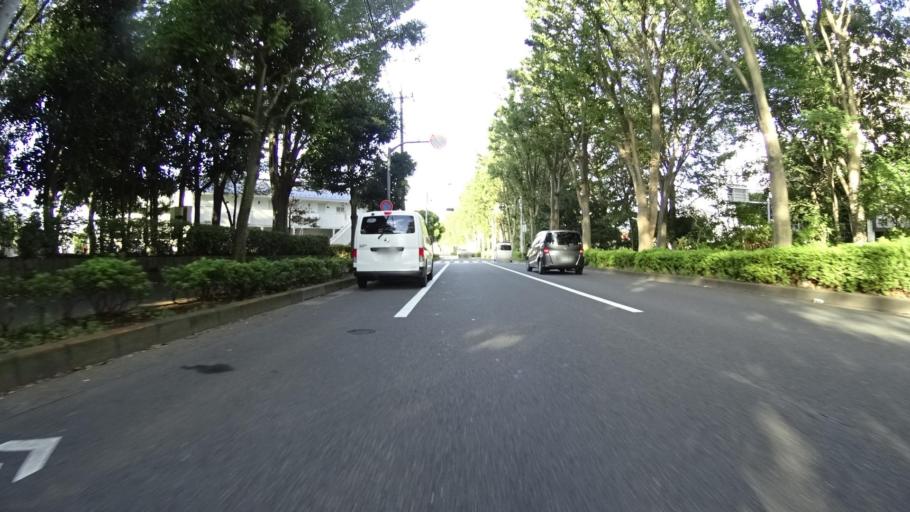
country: JP
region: Tokyo
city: Nishi-Tokyo-shi
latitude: 35.7127
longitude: 139.5410
